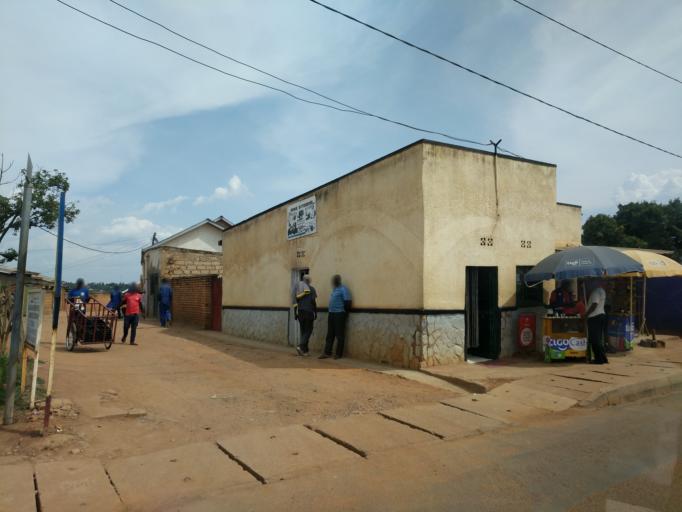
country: RW
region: Kigali
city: Kigali
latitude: -1.9764
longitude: 30.1348
